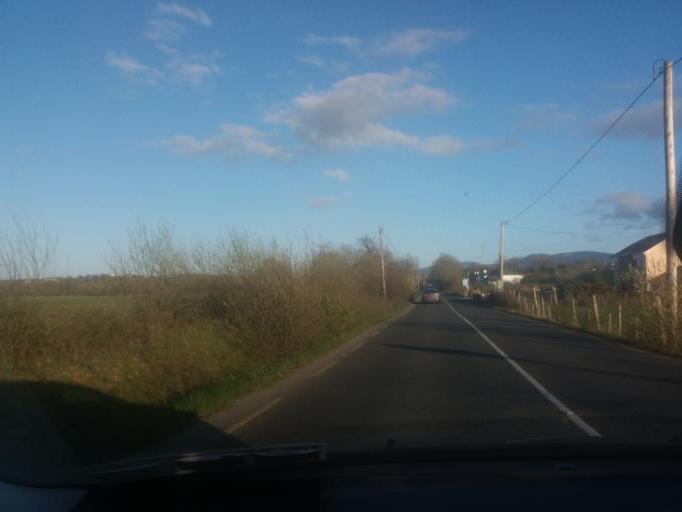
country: IE
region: Munster
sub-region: Ciarrai
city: Cill Airne
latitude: 52.0830
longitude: -9.5920
